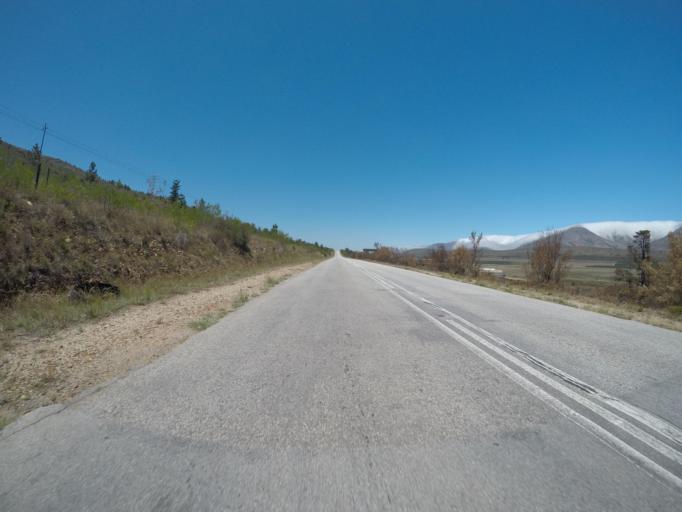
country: ZA
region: Eastern Cape
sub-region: Cacadu District Municipality
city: Kareedouw
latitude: -33.8314
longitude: 23.9021
